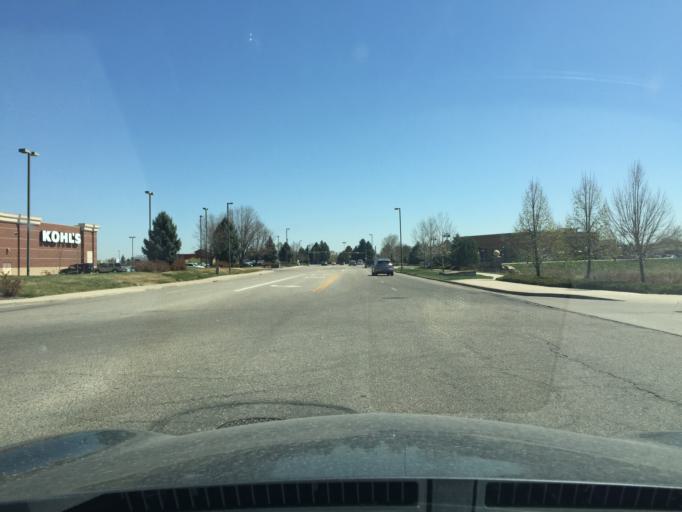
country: US
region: Colorado
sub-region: Boulder County
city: Longmont
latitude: 40.1441
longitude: -105.1344
